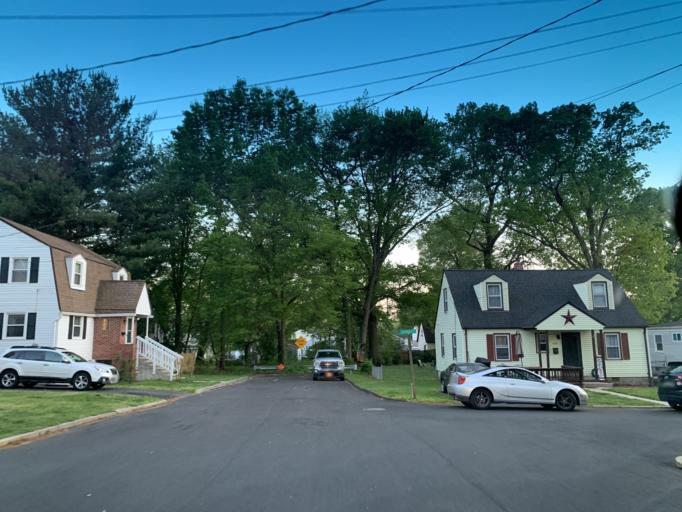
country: US
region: Maryland
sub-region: Harford County
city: Aberdeen
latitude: 39.5064
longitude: -76.1751
